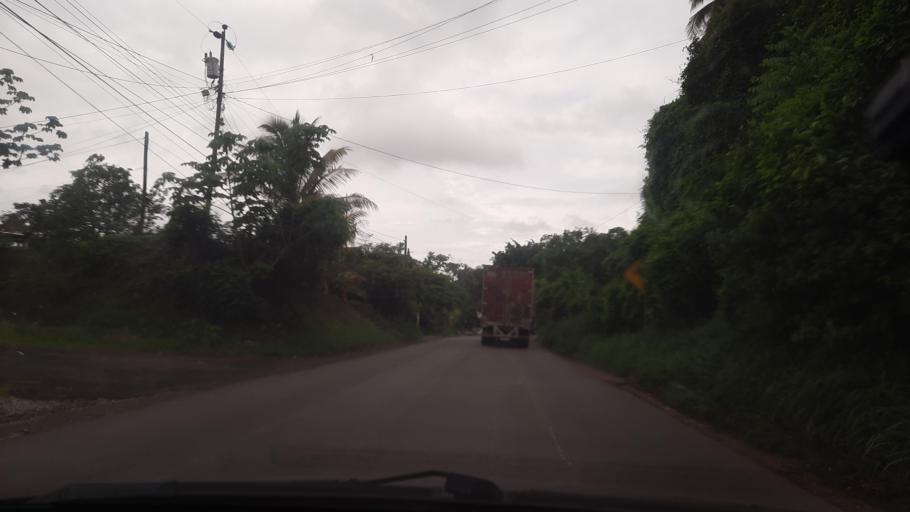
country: GT
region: Izabal
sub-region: Municipio de Los Amates
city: Los Amates
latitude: 15.2764
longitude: -89.0776
